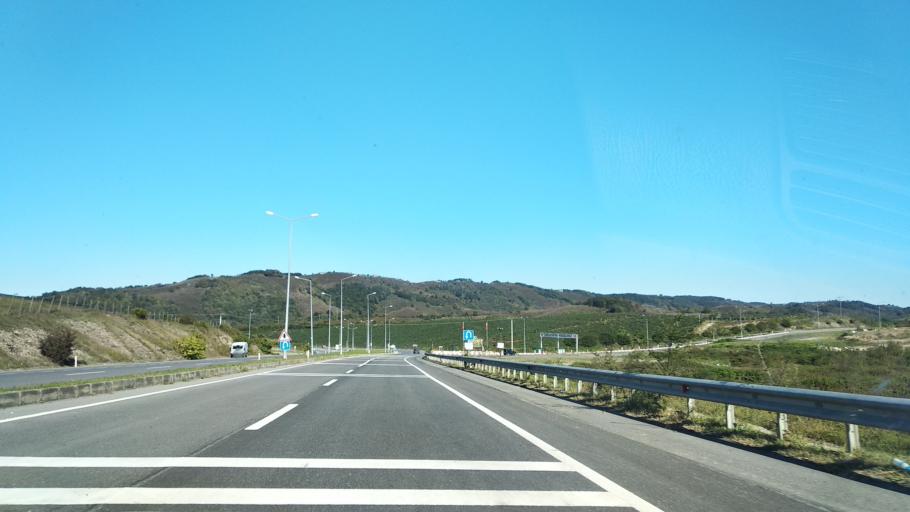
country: TR
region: Sakarya
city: Ortakoy
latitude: 41.0471
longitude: 30.6288
